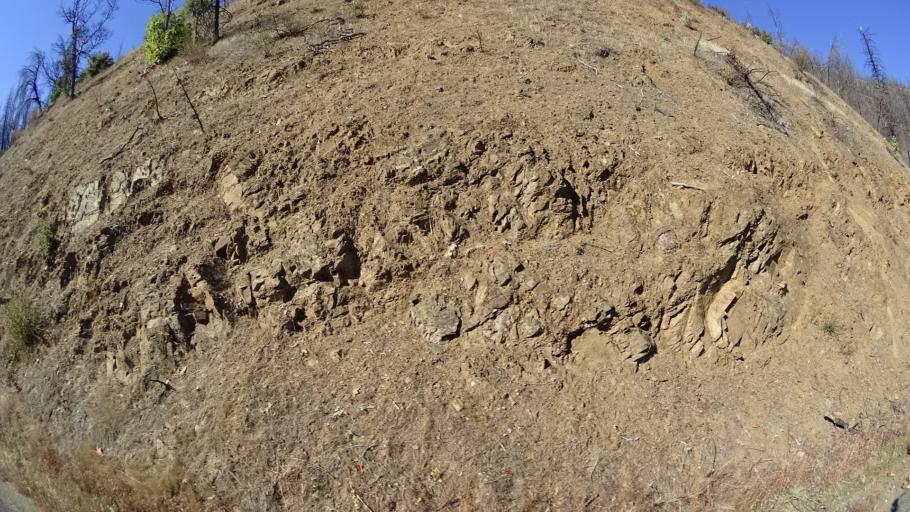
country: US
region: California
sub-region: Siskiyou County
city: Happy Camp
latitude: 41.7227
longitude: -123.0198
